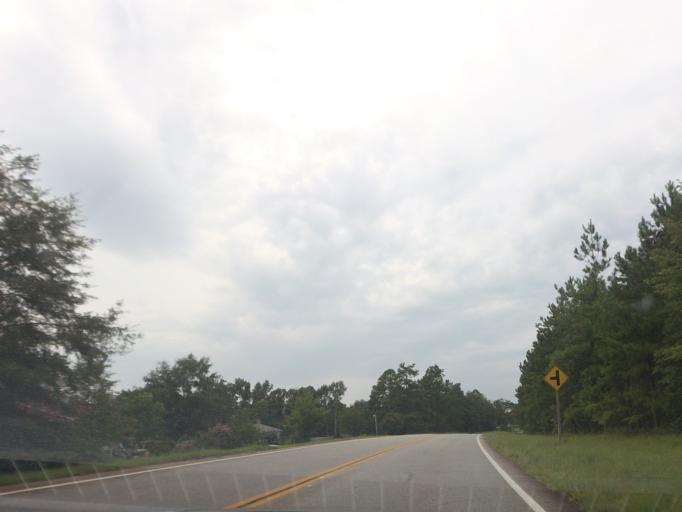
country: US
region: Georgia
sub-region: Twiggs County
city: Jeffersonville
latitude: 32.7230
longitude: -83.4158
